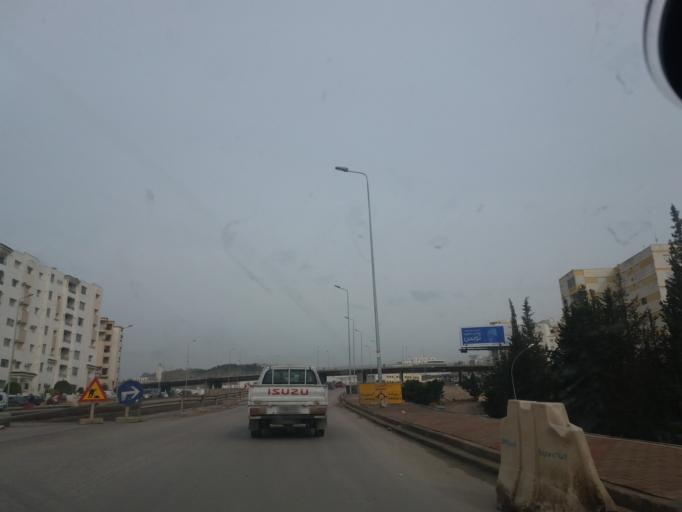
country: TN
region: Tunis
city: Tunis
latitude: 36.8532
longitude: 10.1529
